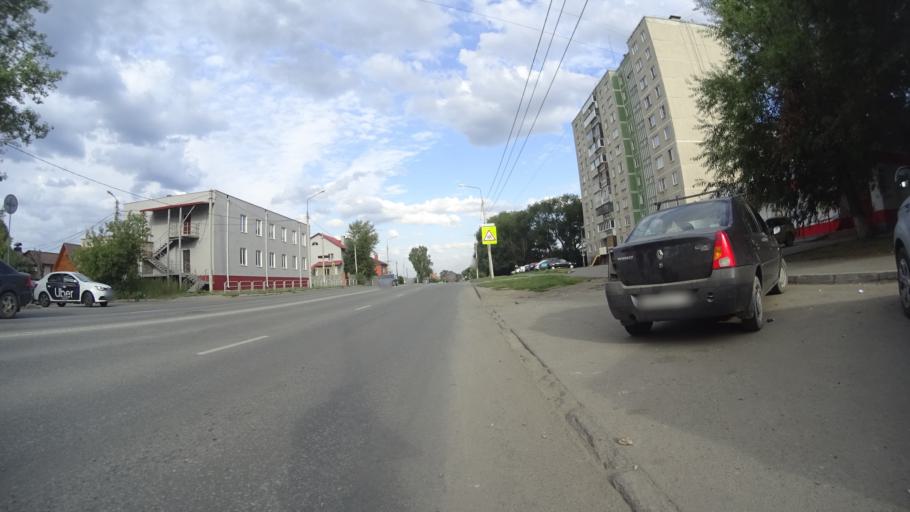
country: RU
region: Chelyabinsk
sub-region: Gorod Chelyabinsk
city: Chelyabinsk
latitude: 55.1985
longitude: 61.3374
